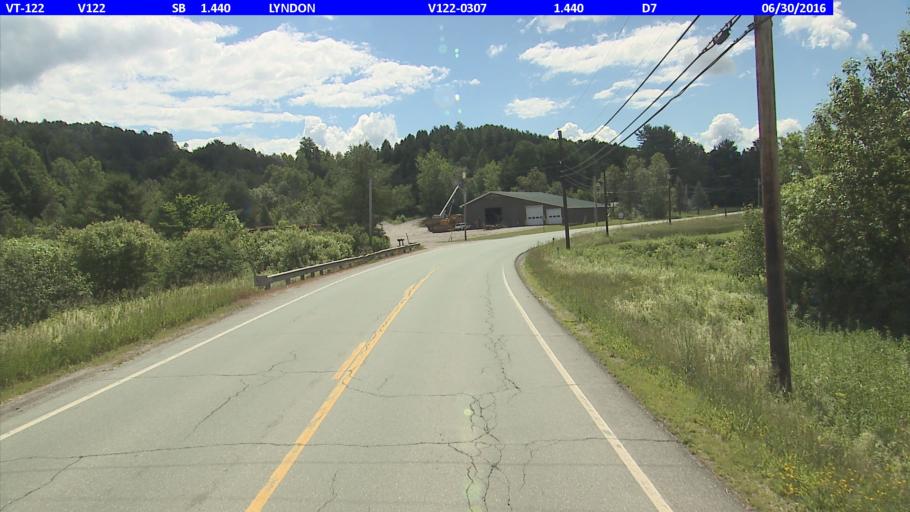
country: US
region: Vermont
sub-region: Caledonia County
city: Lyndonville
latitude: 44.5509
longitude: -72.0232
